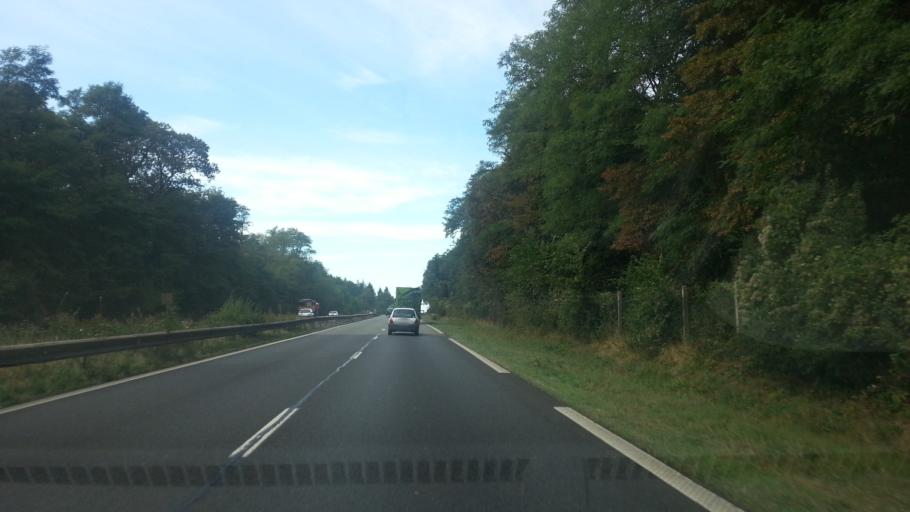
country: FR
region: Picardie
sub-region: Departement de l'Oise
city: Avilly-Saint-Leonard
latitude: 49.2257
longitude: 2.5441
